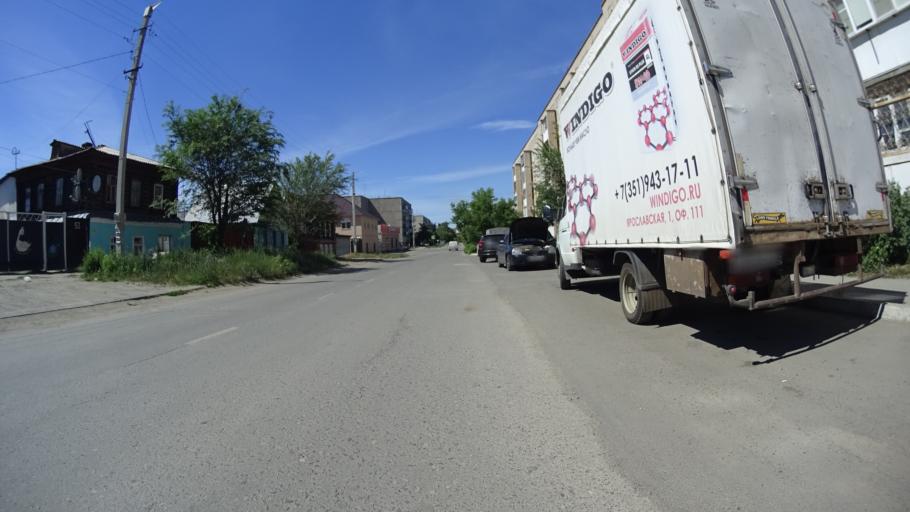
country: RU
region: Chelyabinsk
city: Troitsk
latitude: 54.0903
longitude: 61.5514
